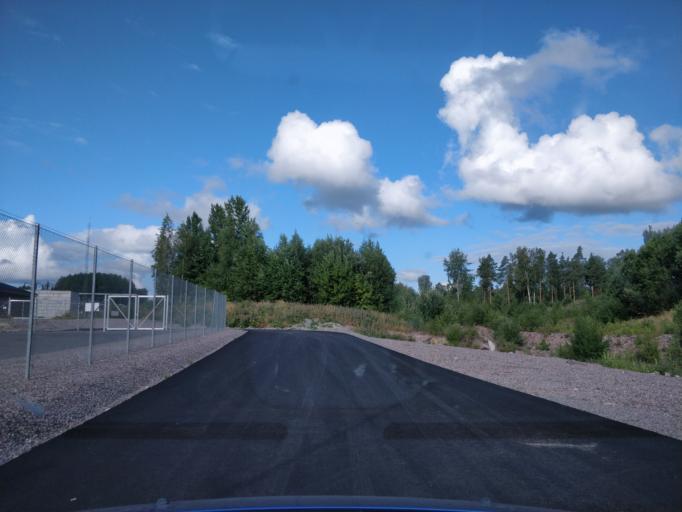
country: FI
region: Uusimaa
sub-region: Helsinki
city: Kerava
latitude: 60.3787
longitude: 25.1535
